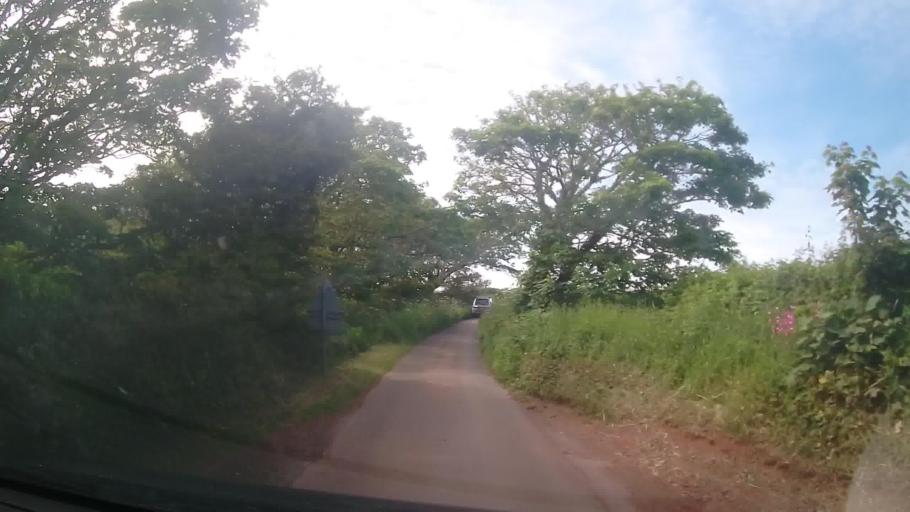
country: GB
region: England
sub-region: Devon
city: Salcombe
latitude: 50.2261
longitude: -3.6575
